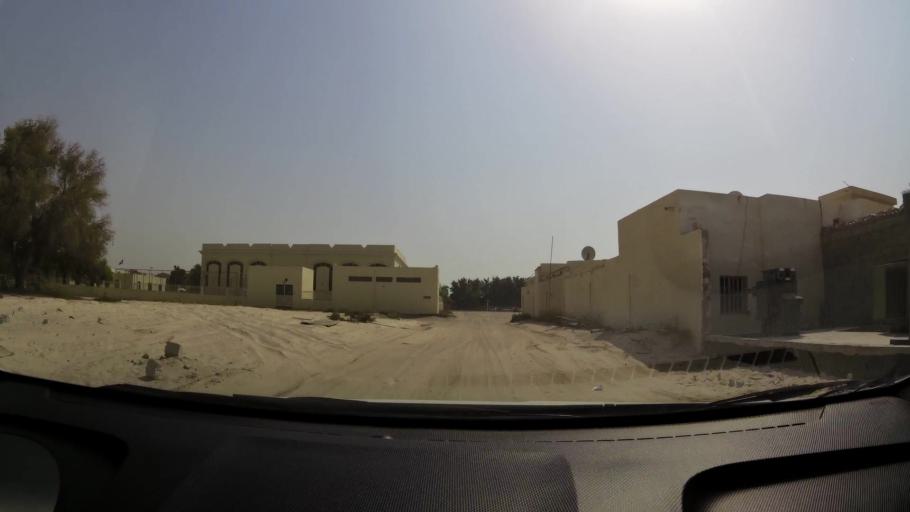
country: AE
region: Ajman
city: Ajman
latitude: 25.3848
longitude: 55.4180
